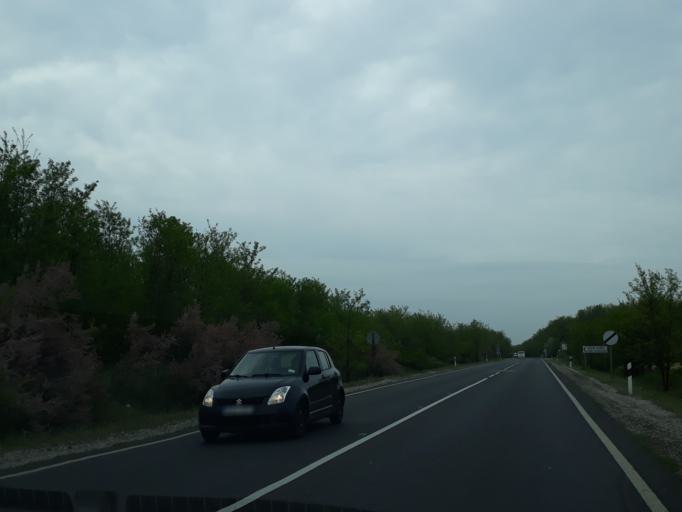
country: HU
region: Szabolcs-Szatmar-Bereg
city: Nyirtass
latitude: 48.1072
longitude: 21.9886
